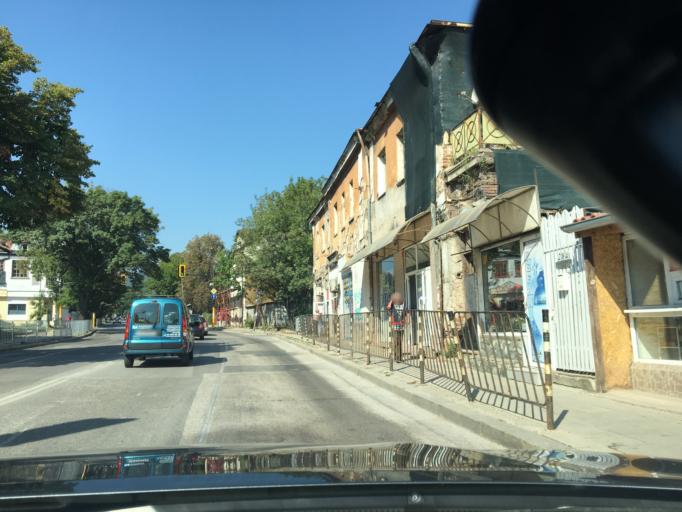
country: BG
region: Sofia-Capital
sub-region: Stolichna Obshtina
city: Sofia
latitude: 42.6590
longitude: 23.2412
